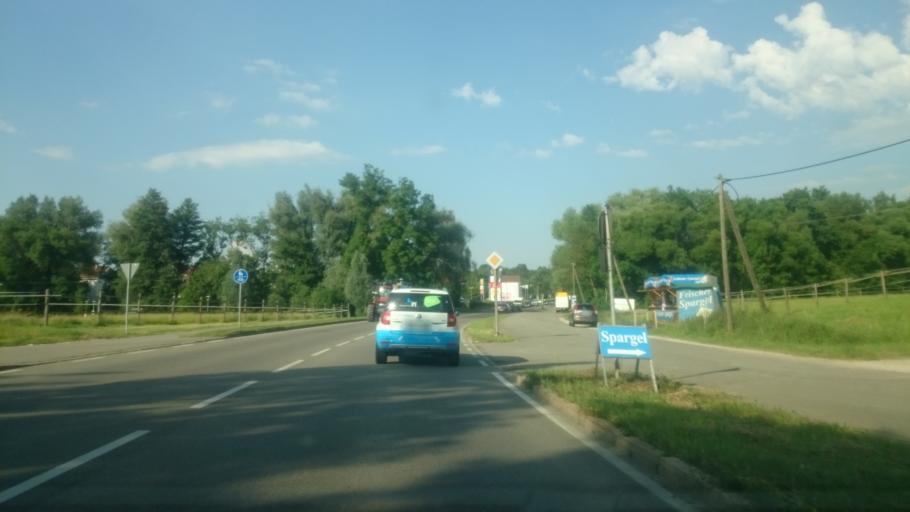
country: DE
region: Baden-Wuerttemberg
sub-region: Tuebingen Region
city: Gomaringen
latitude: 48.4504
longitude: 9.0808
